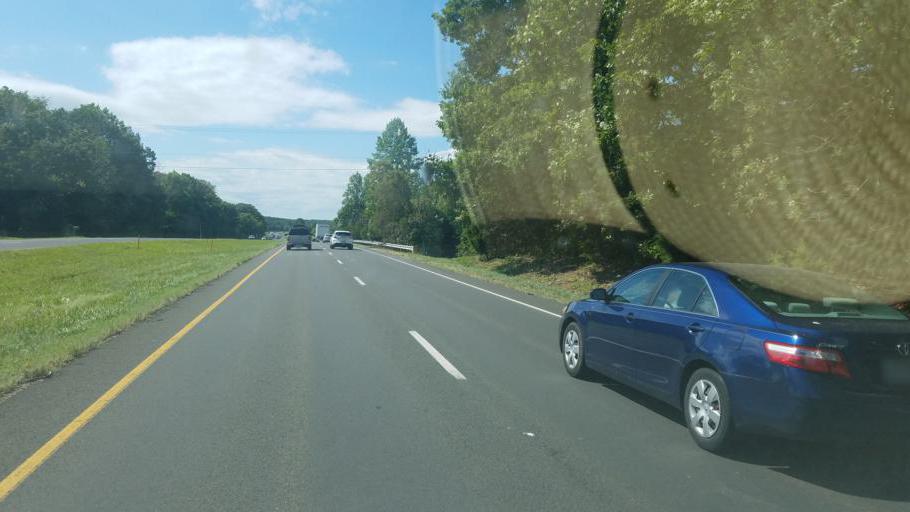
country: US
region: Virginia
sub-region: Fauquier County
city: Bealeton
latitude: 38.4803
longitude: -77.6807
